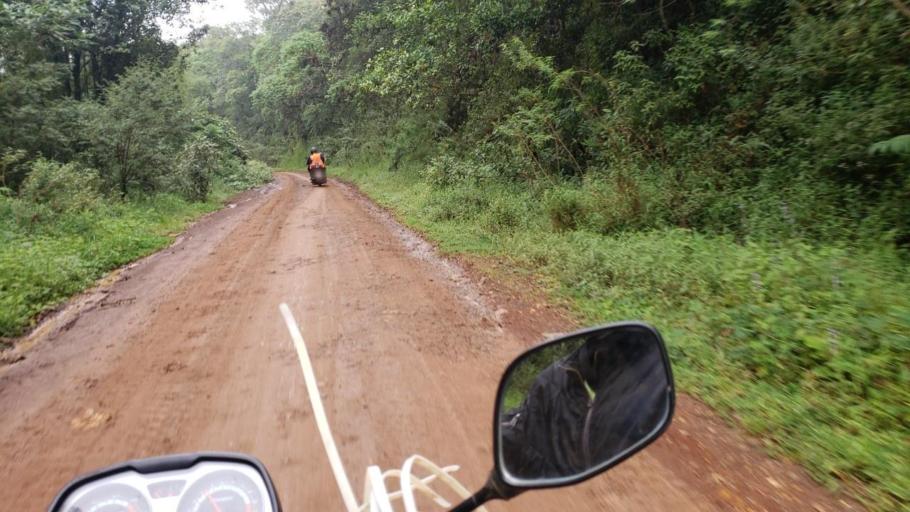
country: CD
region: South Kivu
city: Kabare
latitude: -2.2625
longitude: 28.6579
